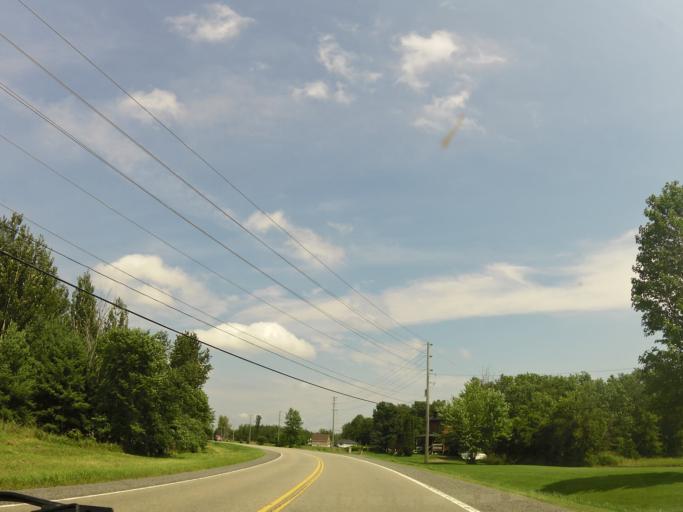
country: CA
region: Ontario
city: Perth
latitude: 44.6629
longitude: -76.3783
